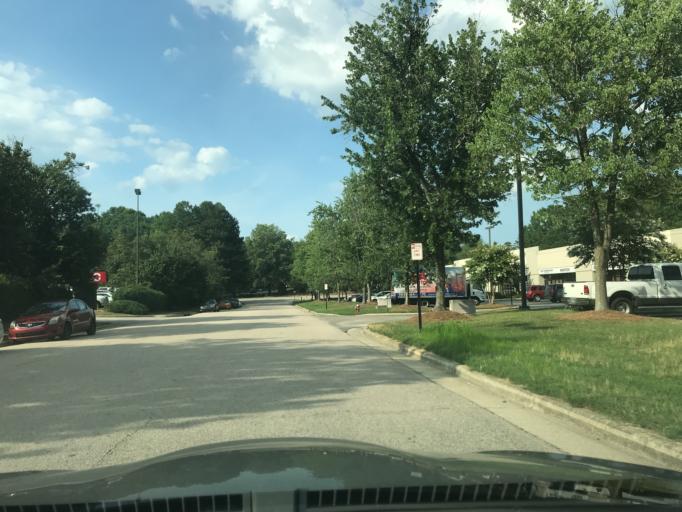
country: US
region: North Carolina
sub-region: Wake County
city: Raleigh
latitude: 35.8578
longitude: -78.5971
